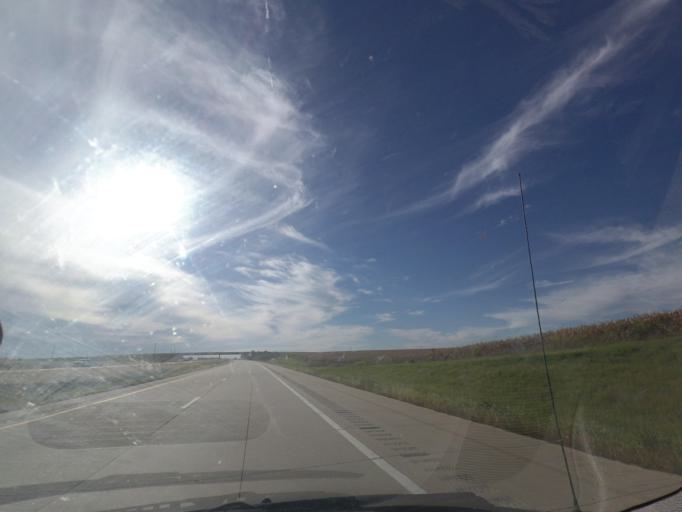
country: US
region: Illinois
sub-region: Sangamon County
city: Riverton
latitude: 39.8396
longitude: -89.4596
